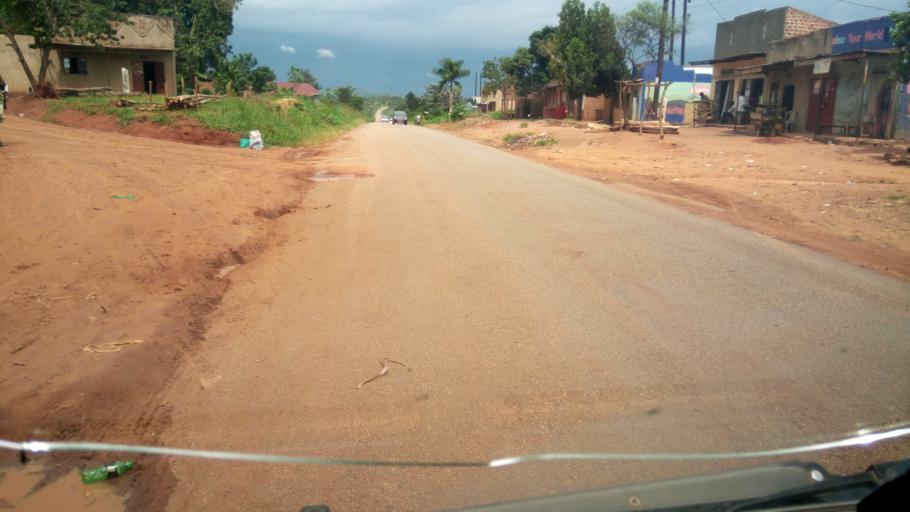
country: UG
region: Central Region
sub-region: Wakiso District
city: Wakiso
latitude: 0.5199
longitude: 32.2725
